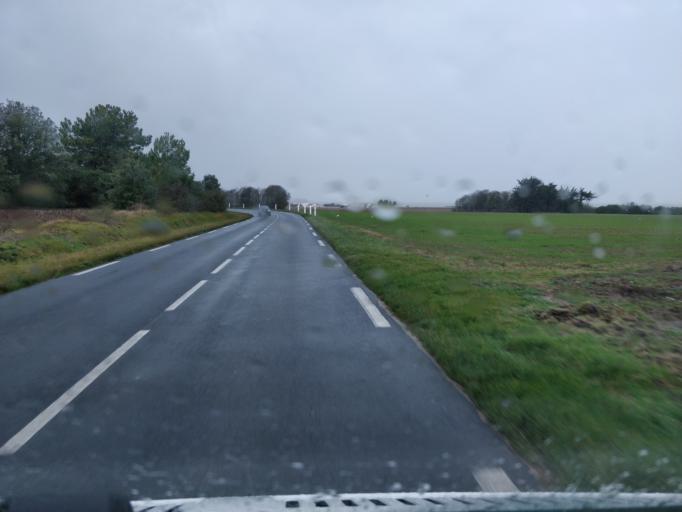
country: FR
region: Poitou-Charentes
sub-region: Departement de la Charente-Maritime
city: La Flotte
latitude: 46.1844
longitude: -1.3026
